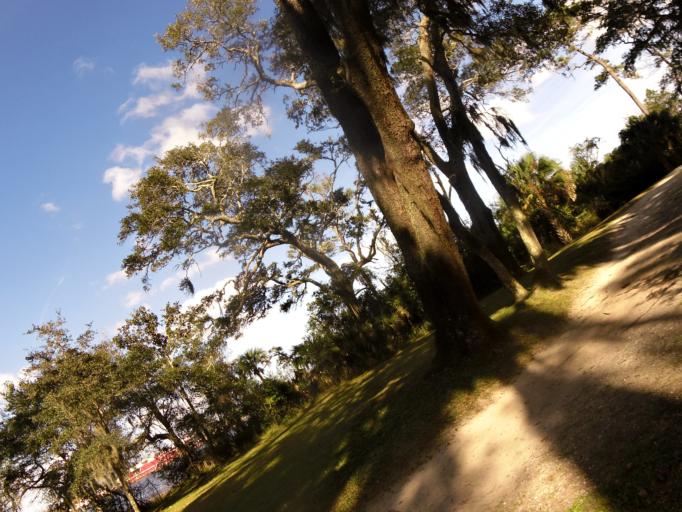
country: US
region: Florida
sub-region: Duval County
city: Atlantic Beach
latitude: 30.3864
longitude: -81.4999
